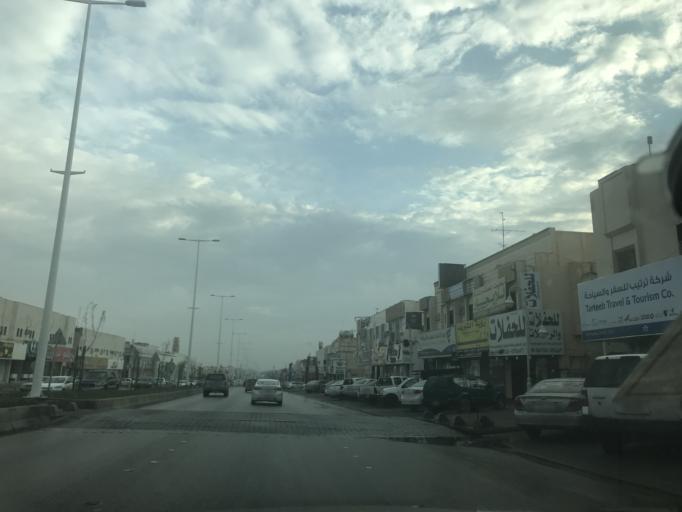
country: SA
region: Ar Riyad
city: Riyadh
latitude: 24.7441
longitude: 46.7535
